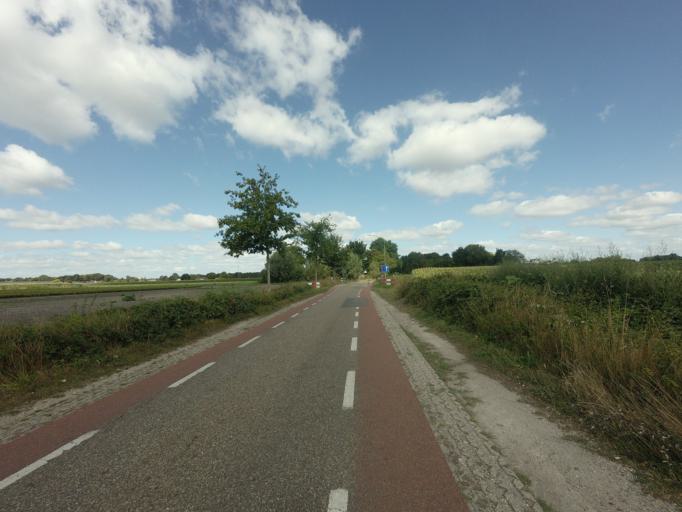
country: NL
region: North Brabant
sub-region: Gemeente Landerd
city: Schaijk
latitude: 51.7409
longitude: 5.6111
